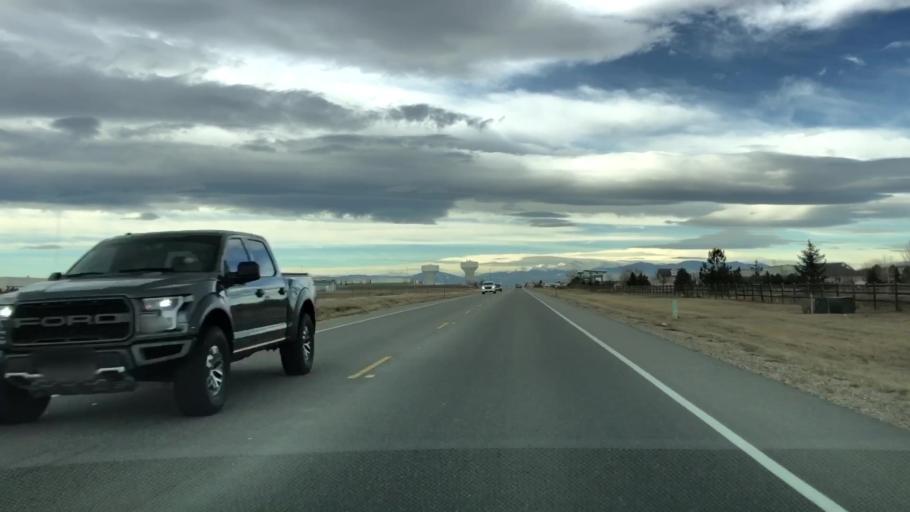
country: US
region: Colorado
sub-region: Weld County
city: Windsor
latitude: 40.4361
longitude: -104.9582
